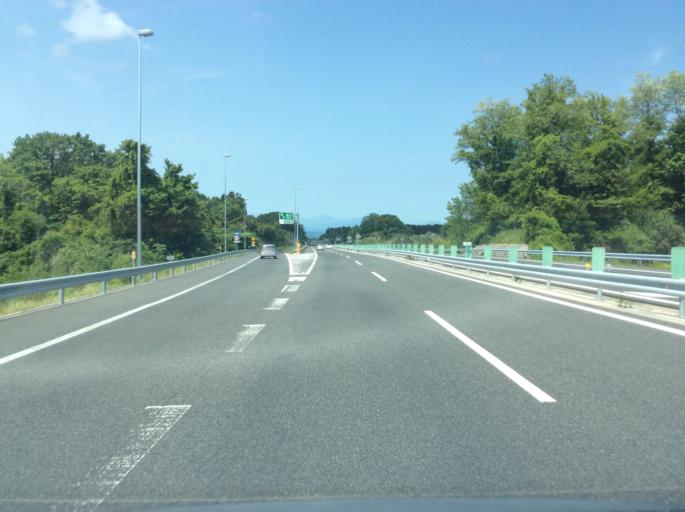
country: JP
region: Fukushima
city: Ishikawa
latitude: 37.2033
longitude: 140.4460
